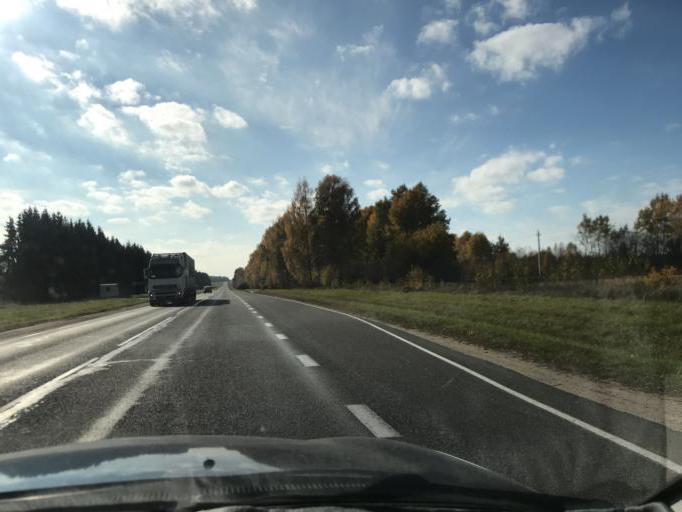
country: BY
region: Grodnenskaya
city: Voranava
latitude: 54.2078
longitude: 25.3503
